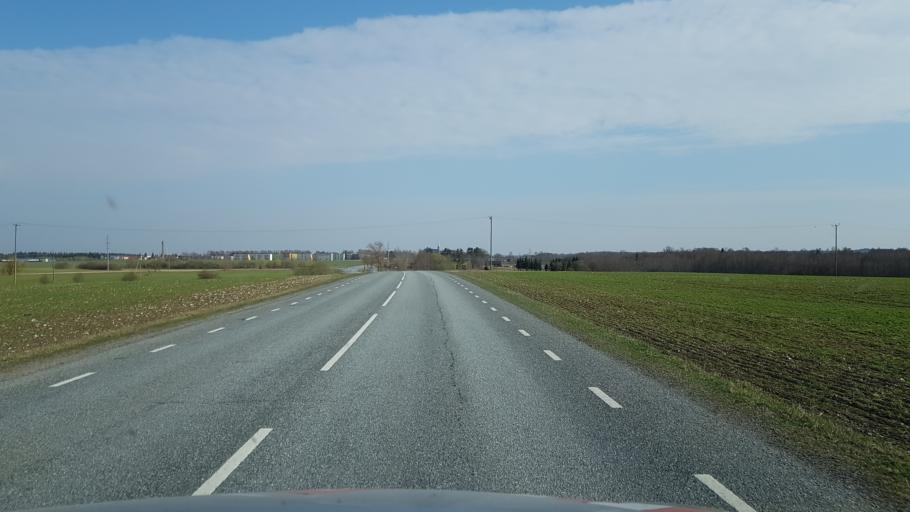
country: EE
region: Laeaene-Virumaa
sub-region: Kadrina vald
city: Kadrina
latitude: 59.3567
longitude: 26.1141
